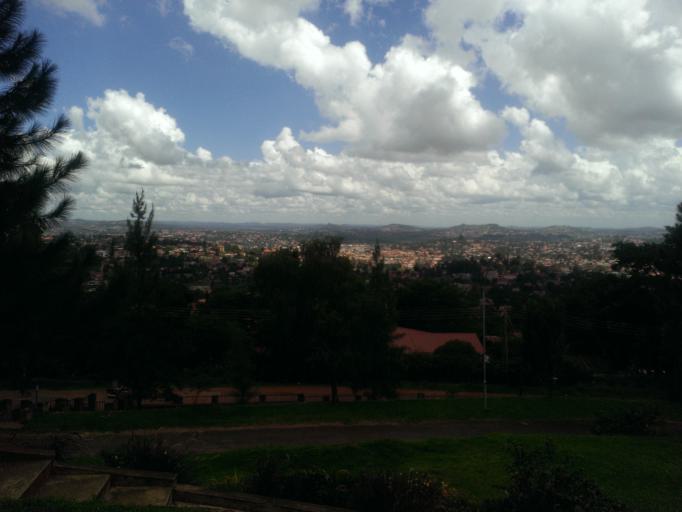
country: UG
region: Central Region
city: Kampala Central Division
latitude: 0.3152
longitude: 32.5593
